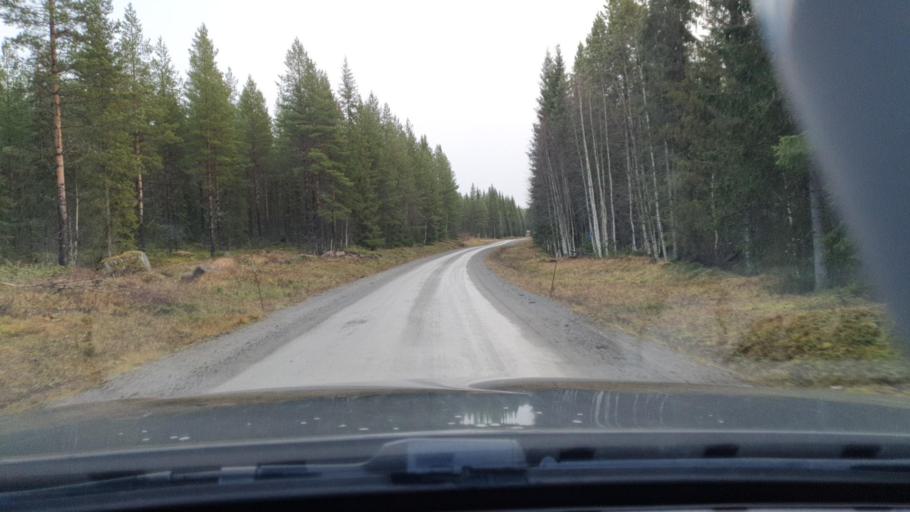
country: SE
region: Jaemtland
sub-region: Stroemsunds Kommun
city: Stroemsund
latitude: 63.5357
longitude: 15.6076
